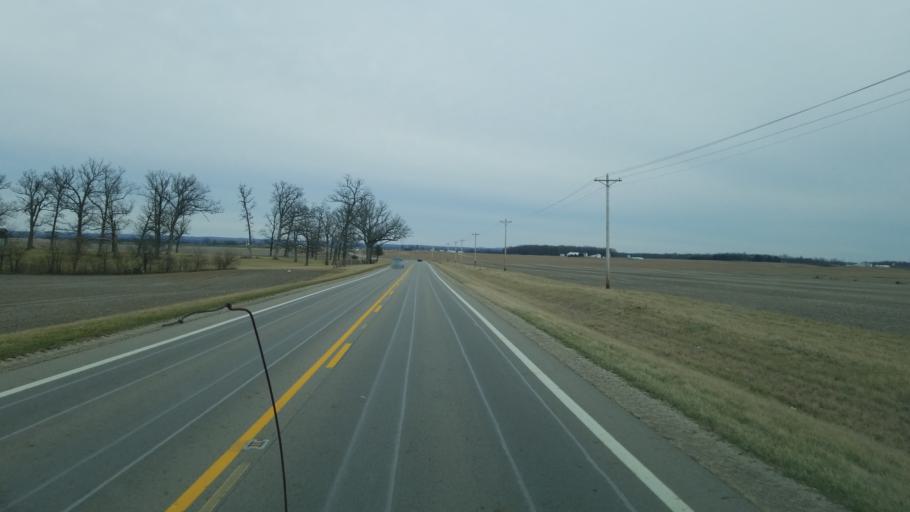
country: US
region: Ohio
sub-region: Pickaway County
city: Logan Elm Village
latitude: 39.5881
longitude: -83.0251
